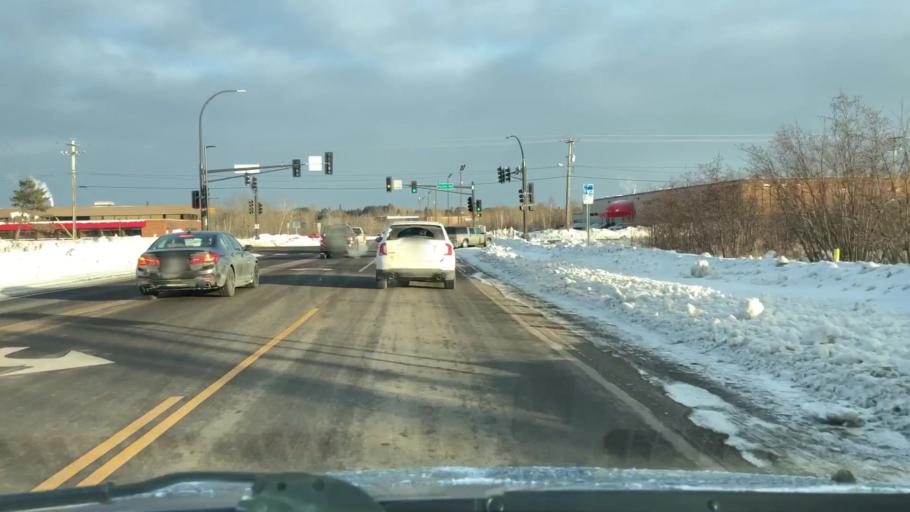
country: US
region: Minnesota
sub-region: Saint Louis County
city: Hermantown
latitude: 46.8130
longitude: -92.1757
